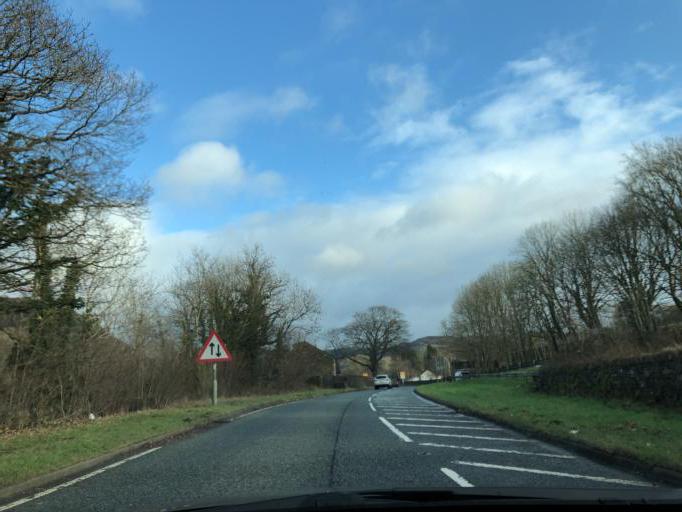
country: GB
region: England
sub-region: Cumbria
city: Grange-over-Sands
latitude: 54.2674
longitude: -2.9771
